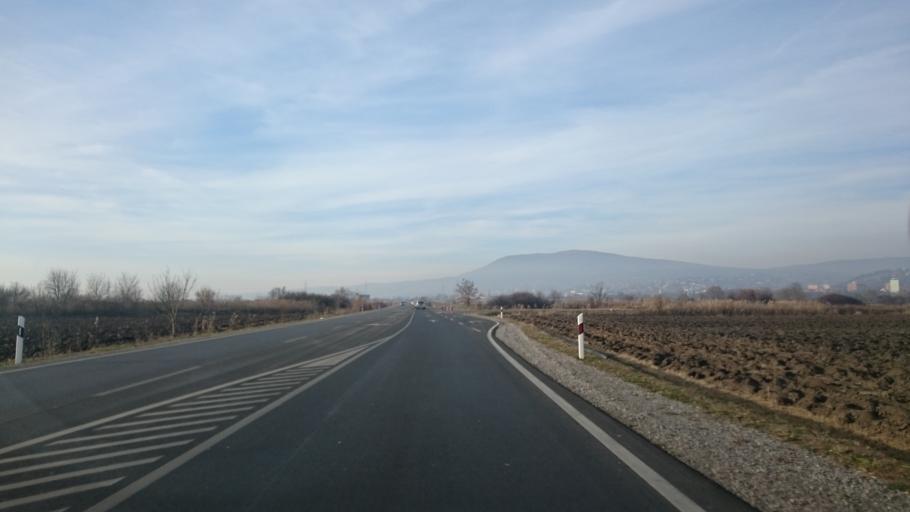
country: HU
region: Baranya
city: Pecs
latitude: 46.0501
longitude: 18.2026
